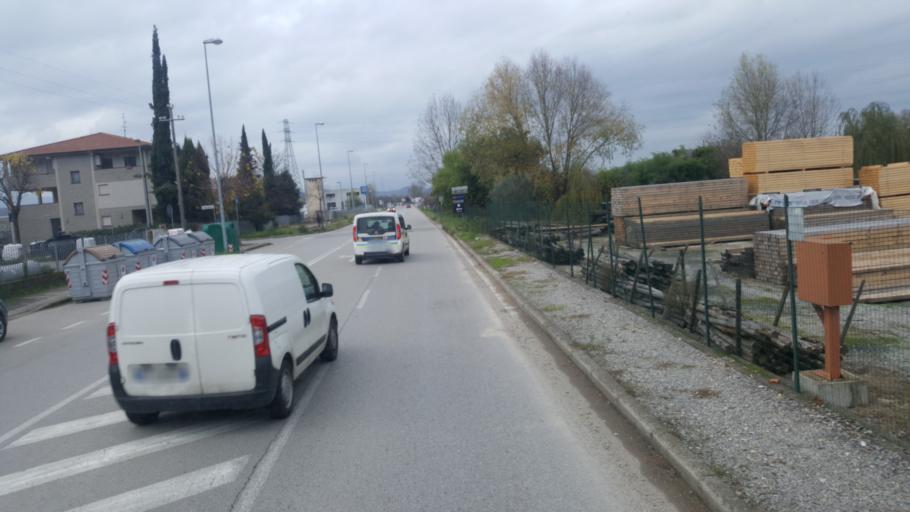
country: IT
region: Tuscany
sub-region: Province of Arezzo
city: Montevarchi
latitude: 43.5405
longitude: 11.5620
